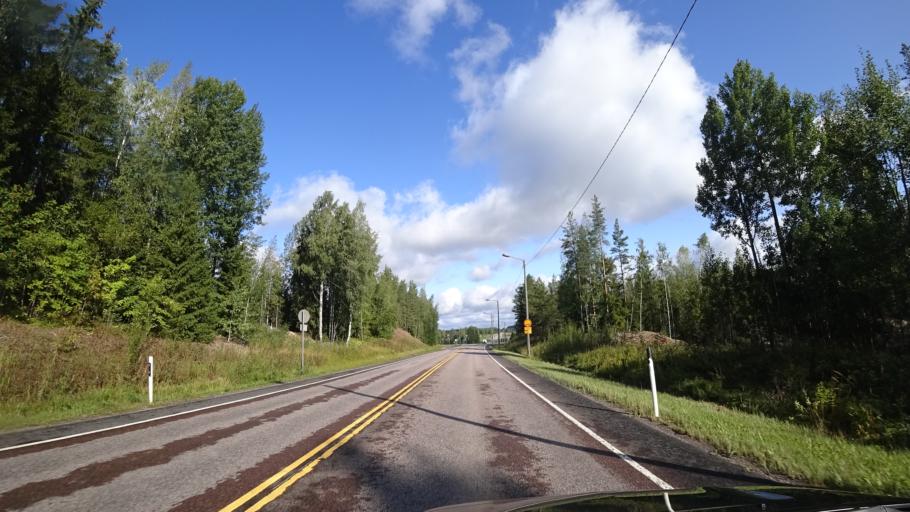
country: FI
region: Uusimaa
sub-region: Helsinki
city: Nurmijaervi
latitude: 60.5091
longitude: 24.9285
